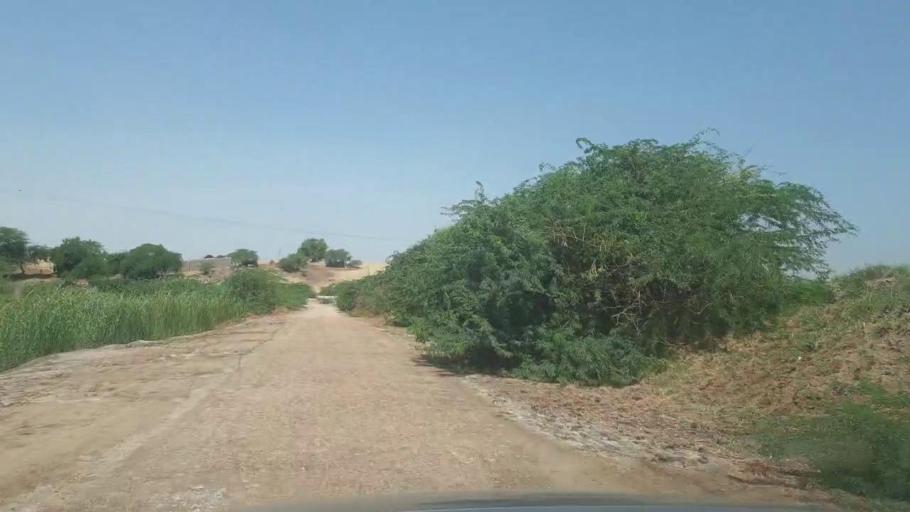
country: PK
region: Sindh
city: Kot Diji
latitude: 27.3253
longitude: 69.0129
